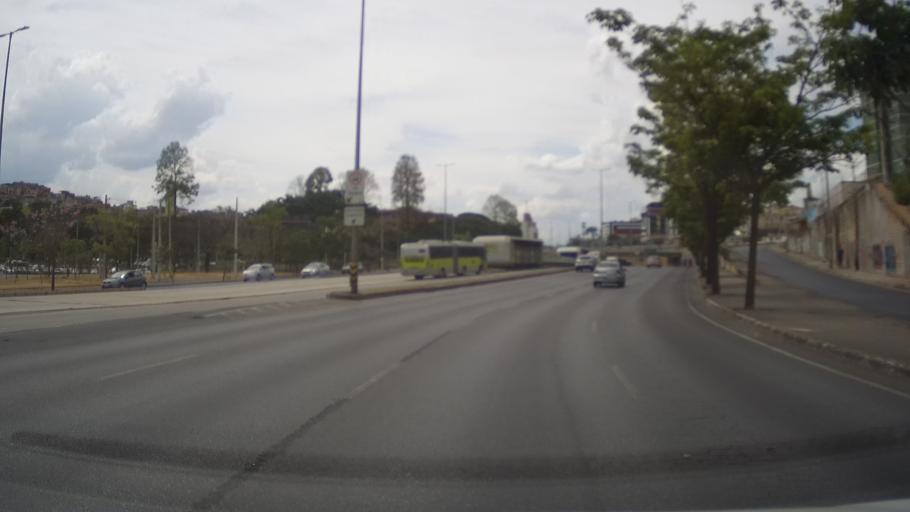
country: BR
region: Minas Gerais
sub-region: Belo Horizonte
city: Belo Horizonte
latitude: -19.9049
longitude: -43.9441
